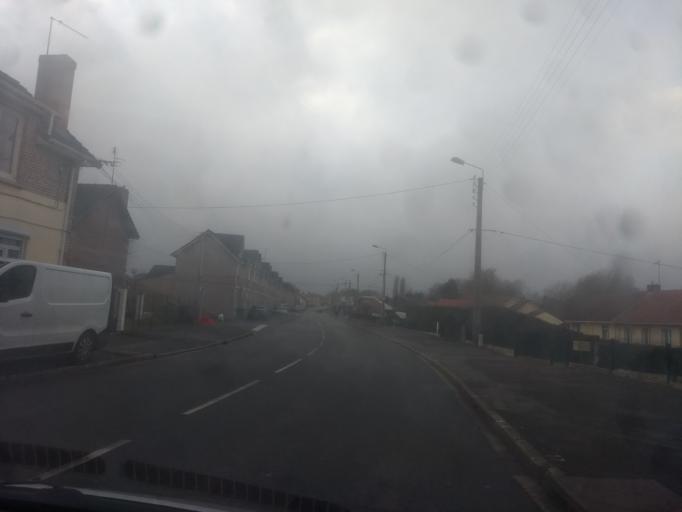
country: FR
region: Nord-Pas-de-Calais
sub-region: Departement du Pas-de-Calais
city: Lievin
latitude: 50.4110
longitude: 2.7889
